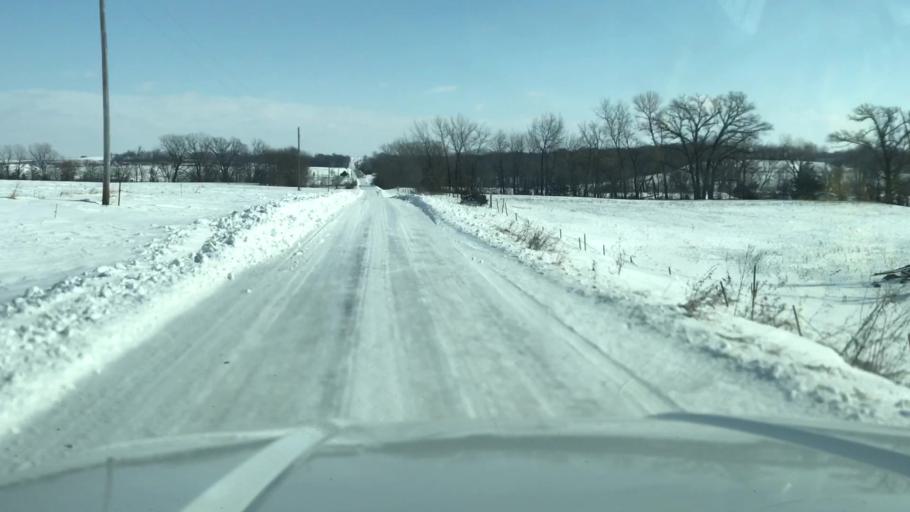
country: US
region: Missouri
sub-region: Nodaway County
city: Maryville
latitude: 40.3865
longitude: -94.6740
